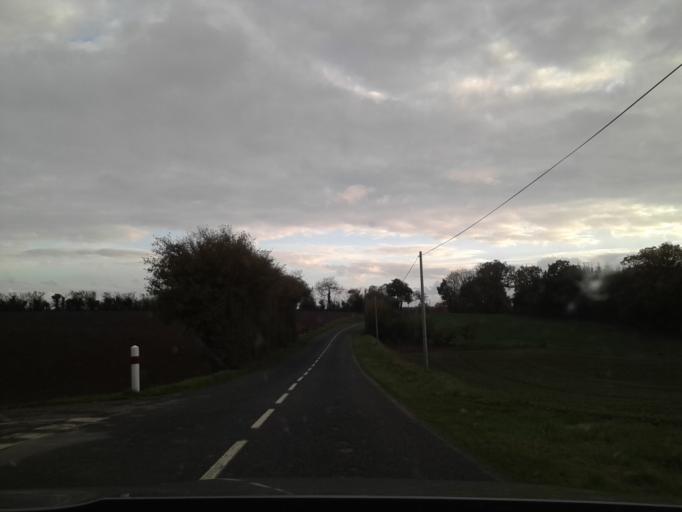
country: FR
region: Lower Normandy
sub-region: Departement du Calvados
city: Le Theil-Bocage
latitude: 48.8751
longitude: -0.6932
